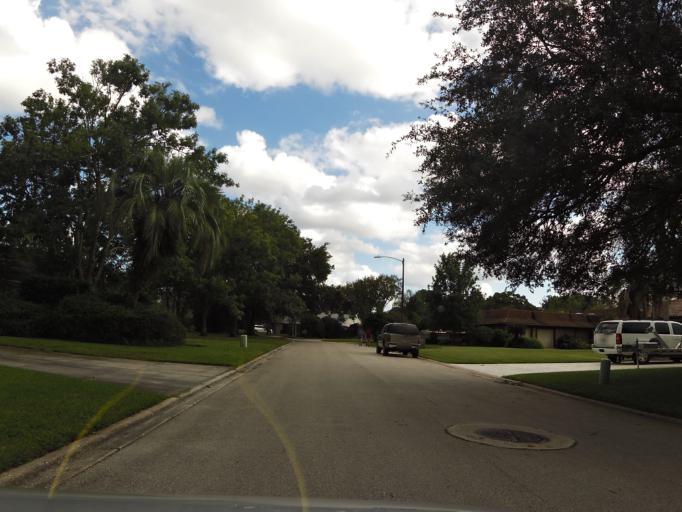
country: US
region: Florida
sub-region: Clay County
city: Bellair-Meadowbrook Terrace
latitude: 30.2528
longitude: -81.7071
